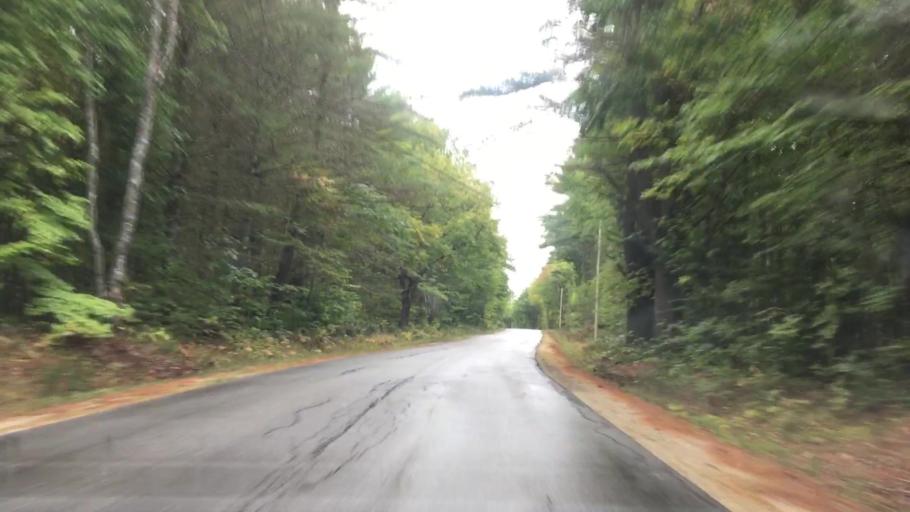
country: US
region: Maine
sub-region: Cumberland County
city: Harrison
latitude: 44.0430
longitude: -70.6115
